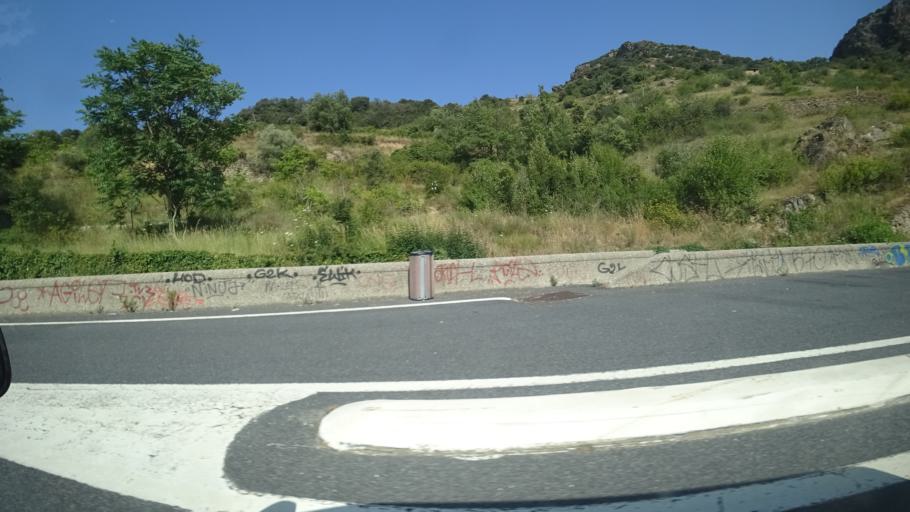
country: FR
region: Languedoc-Roussillon
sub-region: Departement des Pyrenees-Orientales
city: Vernet-les-Bains
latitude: 42.5726
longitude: 2.3372
